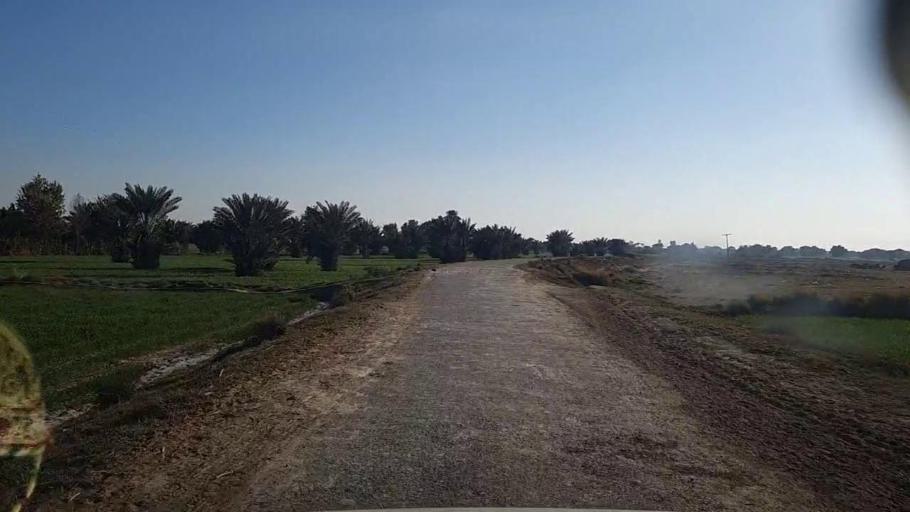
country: PK
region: Sindh
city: Khairpur
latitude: 28.0095
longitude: 69.7212
